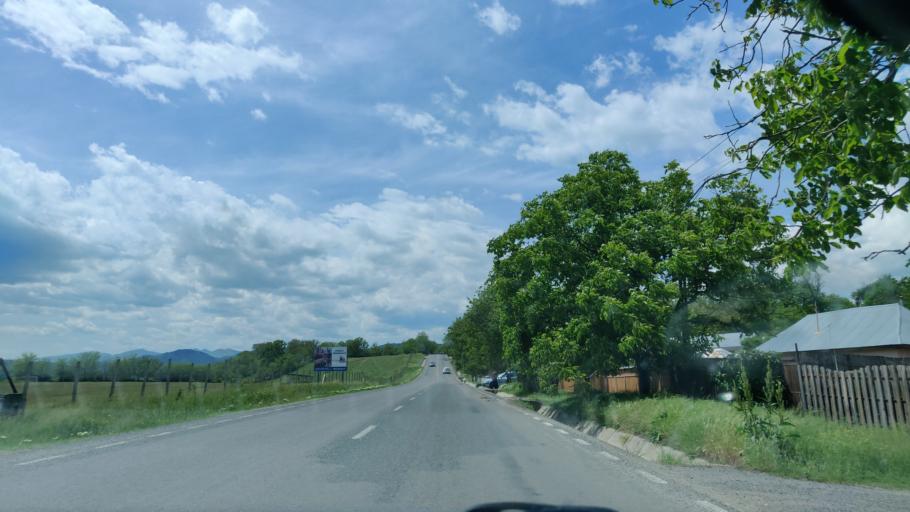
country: RO
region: Vrancea
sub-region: Comuna Vidra
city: Vidra
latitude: 45.8980
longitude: 26.8776
